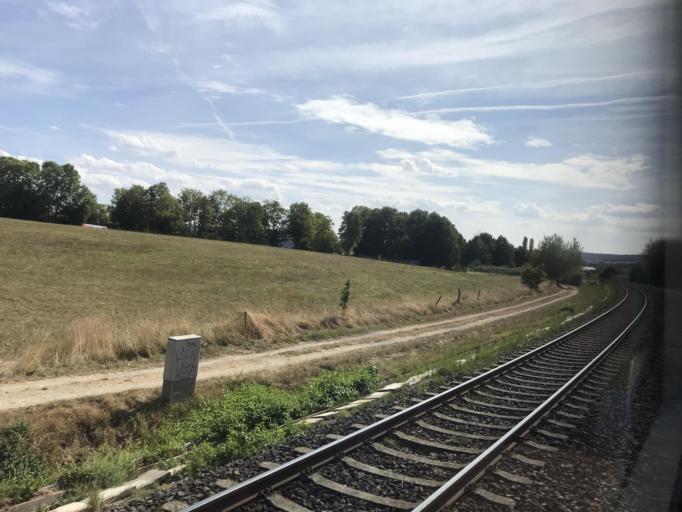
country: DE
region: Hesse
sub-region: Regierungsbezirk Giessen
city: Limburg an der Lahn
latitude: 50.3864
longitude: 8.0385
